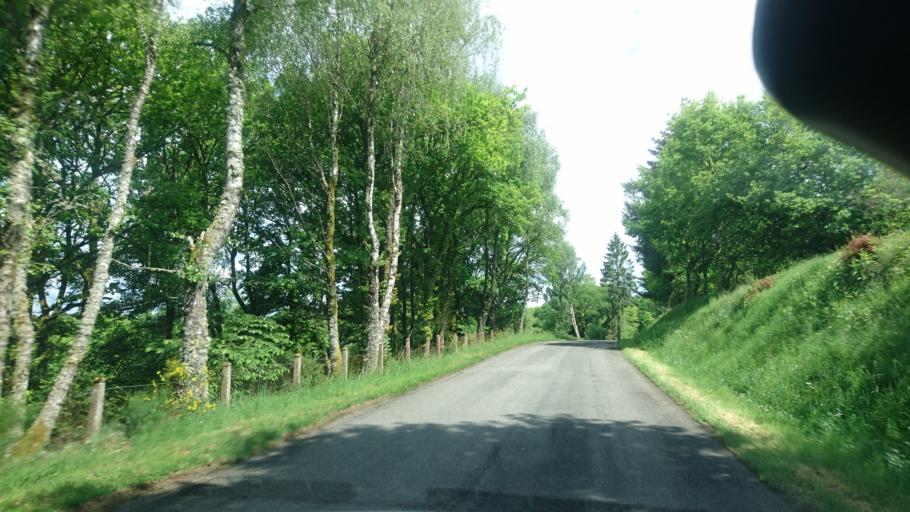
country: FR
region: Limousin
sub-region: Departement de la Haute-Vienne
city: Peyrat-le-Chateau
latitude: 45.7775
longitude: 1.8735
